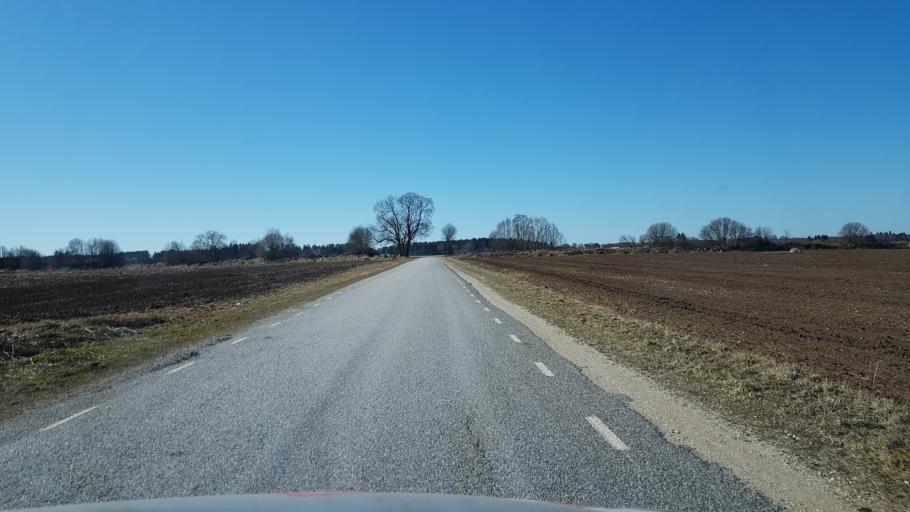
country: EE
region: Laeaene-Virumaa
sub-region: Viru-Nigula vald
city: Kunda
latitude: 59.4008
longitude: 26.5496
